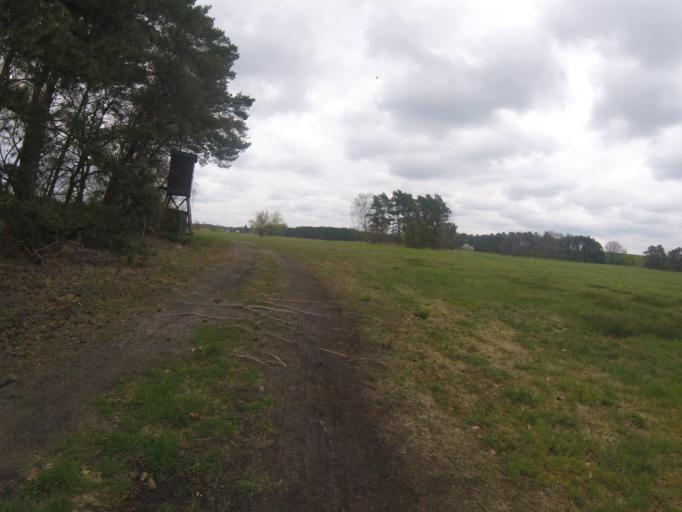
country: DE
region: Brandenburg
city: Mittenwalde
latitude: 52.2637
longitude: 13.5897
